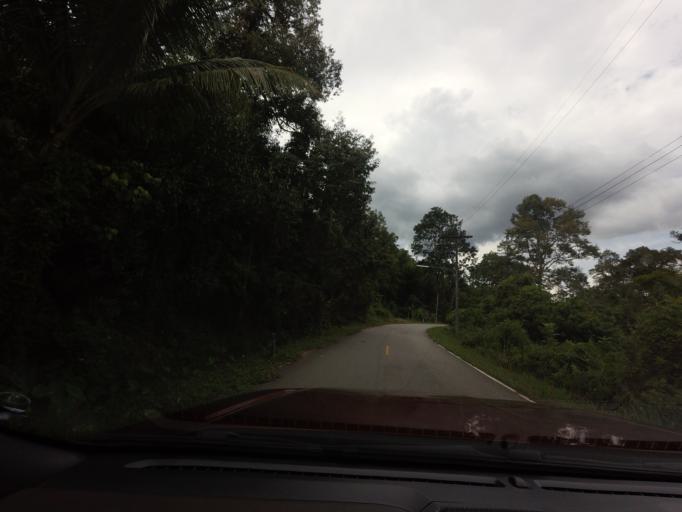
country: TH
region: Narathiwat
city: Sukhirin
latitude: 5.9901
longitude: 101.7055
